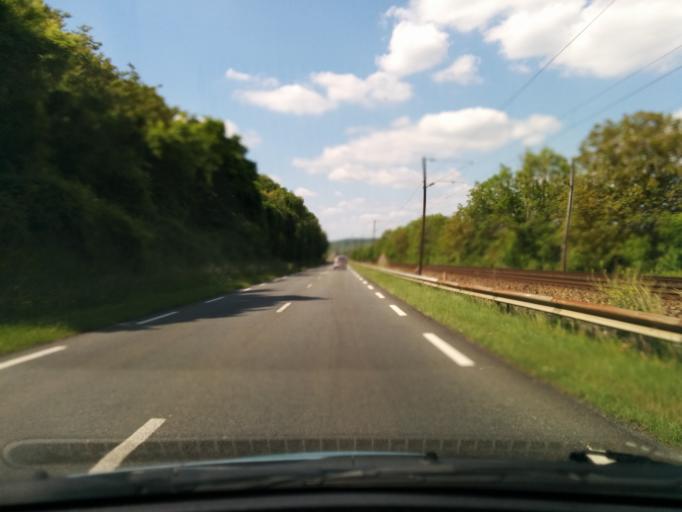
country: FR
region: Ile-de-France
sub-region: Departement des Yvelines
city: Limetz-Villez
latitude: 49.0572
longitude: 1.5261
